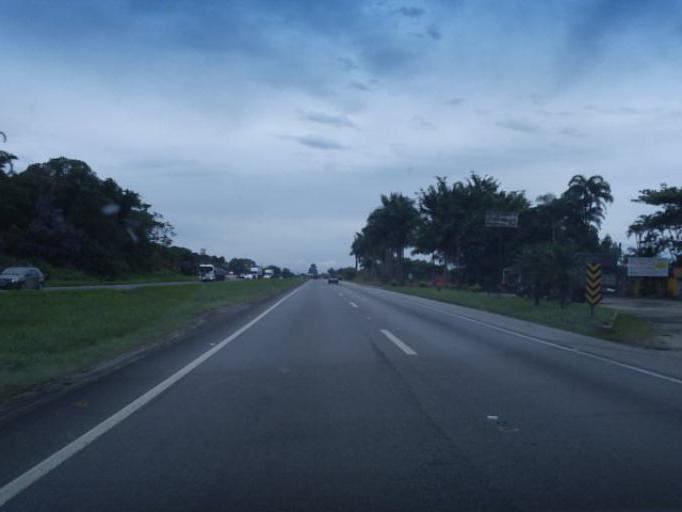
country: BR
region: Sao Paulo
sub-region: Juquia
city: Juquia
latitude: -24.3547
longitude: -47.6755
